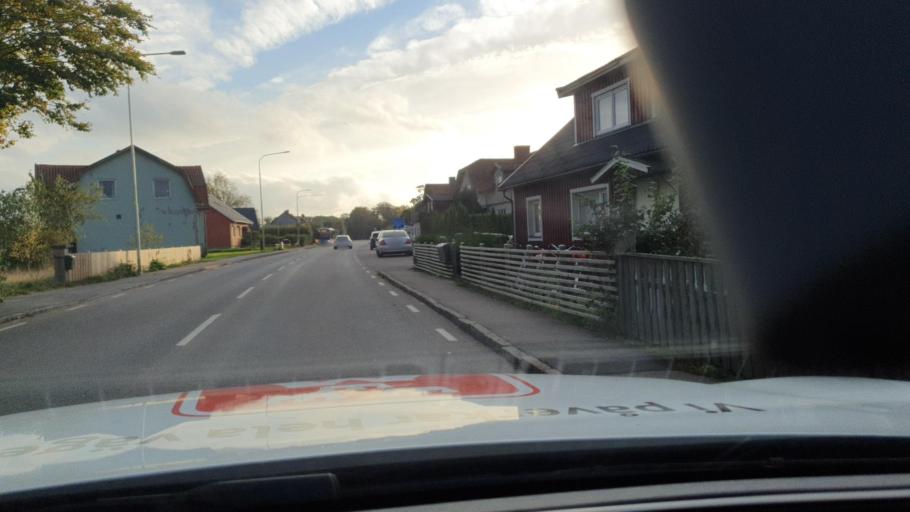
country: SE
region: Halland
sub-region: Laholms Kommun
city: Laholm
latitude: 56.4686
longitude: 13.0259
